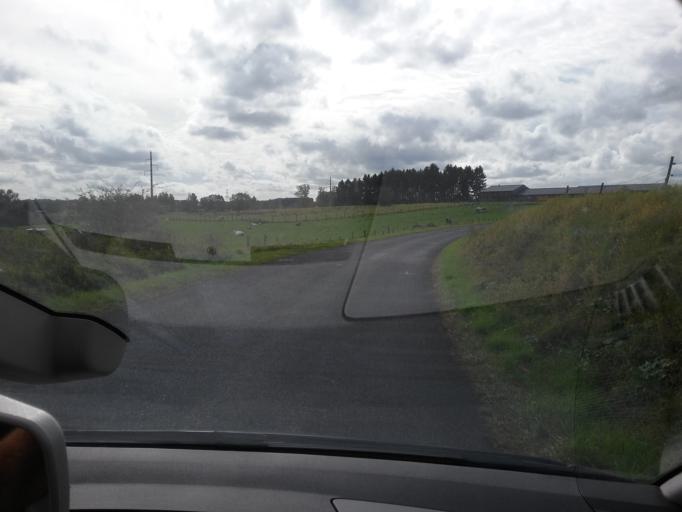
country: BE
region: Wallonia
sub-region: Province du Luxembourg
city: Arlon
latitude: 49.6984
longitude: 5.7783
